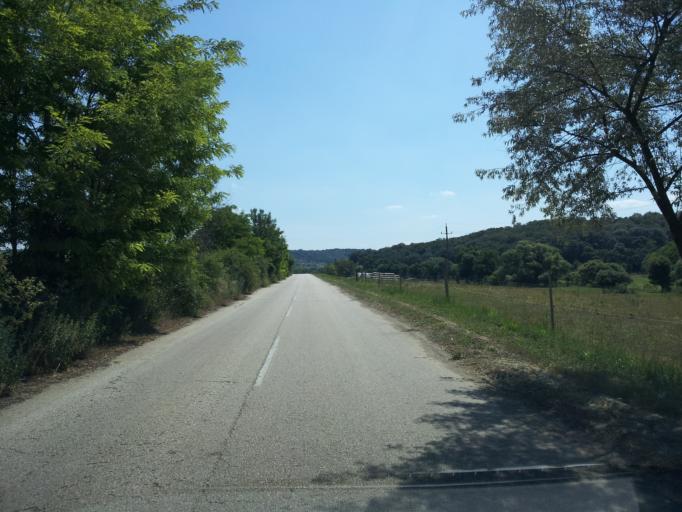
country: HU
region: Fejer
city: Many
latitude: 47.5299
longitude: 18.5788
